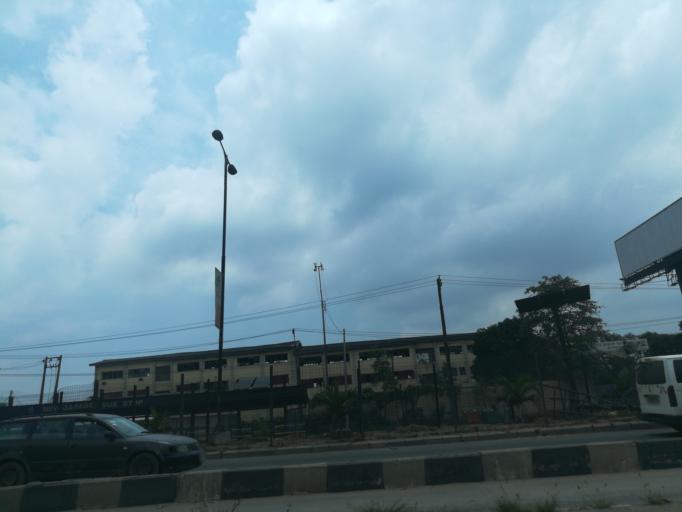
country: NG
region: Lagos
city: Ojota
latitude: 6.5843
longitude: 3.3762
